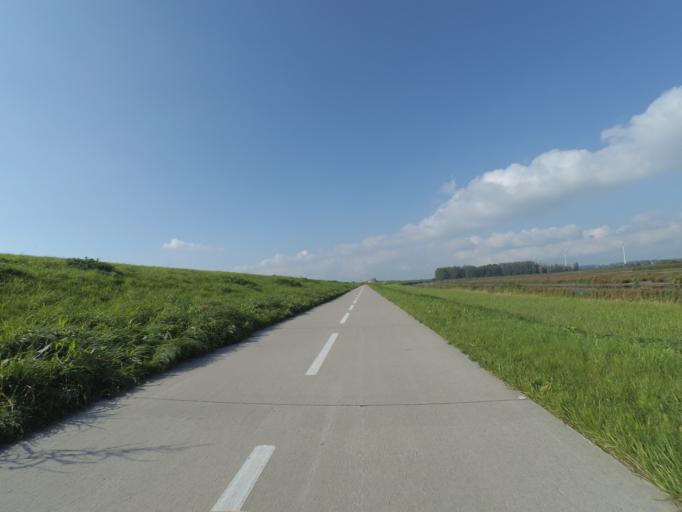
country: NL
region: Flevoland
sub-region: Gemeente Zeewolde
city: Zeewolde
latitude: 52.3661
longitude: 5.5702
